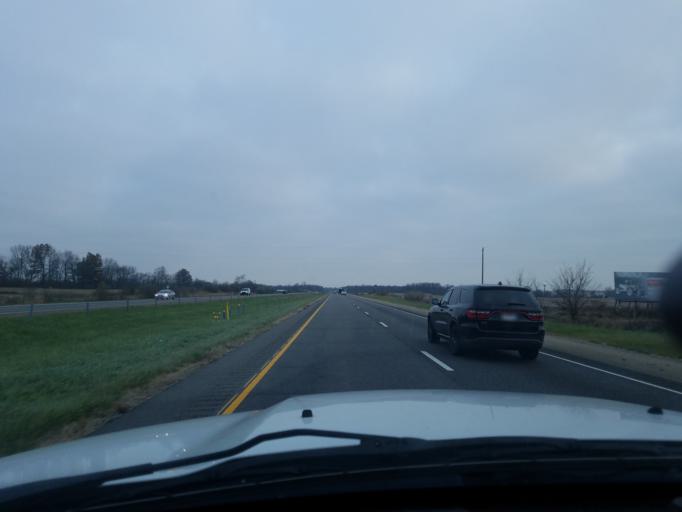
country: US
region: Indiana
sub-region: Delaware County
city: Yorktown
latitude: 40.1995
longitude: -85.5609
